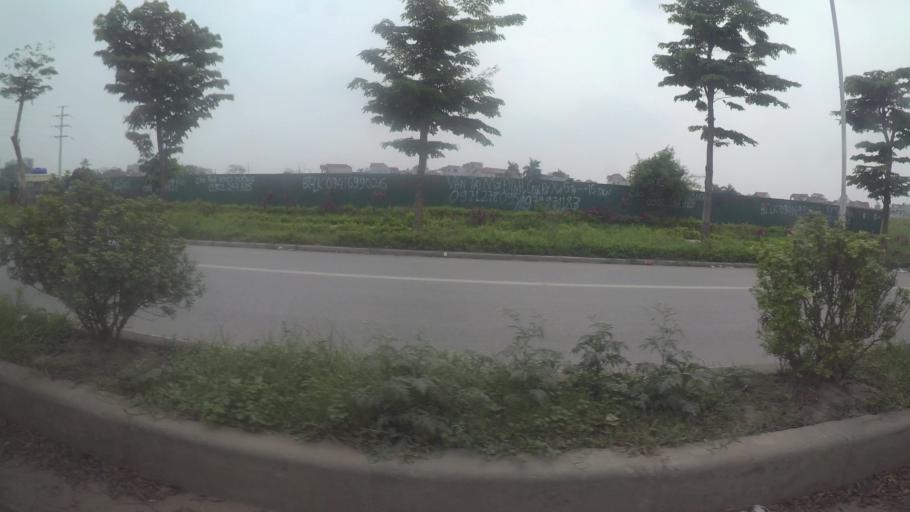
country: VN
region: Ha Noi
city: Cau Dien
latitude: 21.0375
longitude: 105.7471
